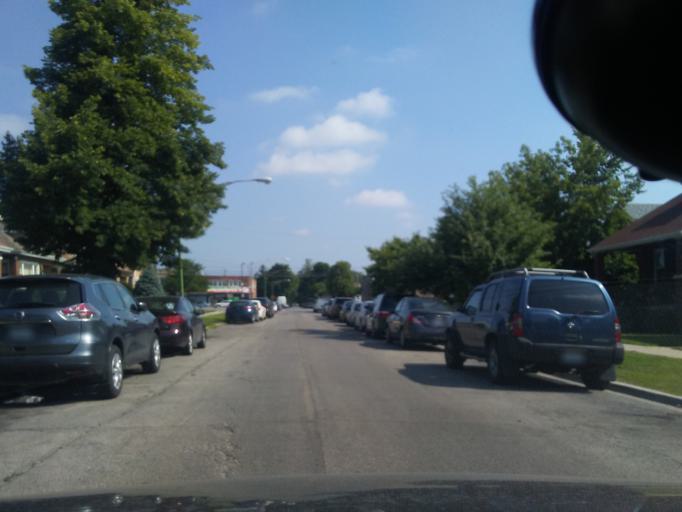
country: US
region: Illinois
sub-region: Cook County
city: Elmwood Park
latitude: 41.9300
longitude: -87.7687
